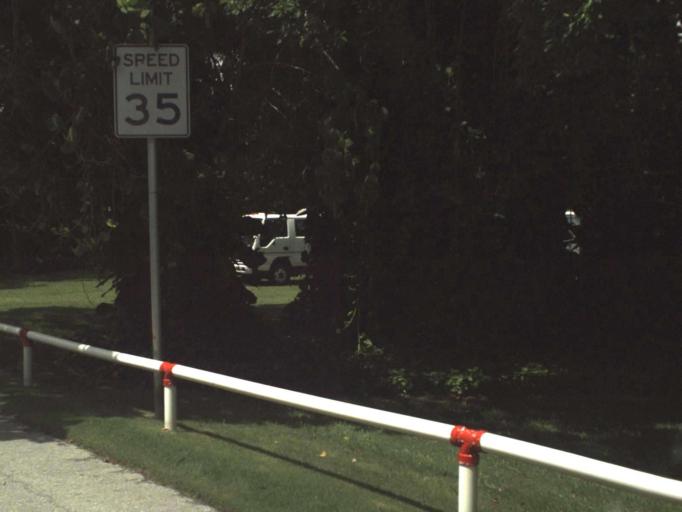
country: US
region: Florida
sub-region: Broward County
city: Hillsboro Beach
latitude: 26.2917
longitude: -80.0793
